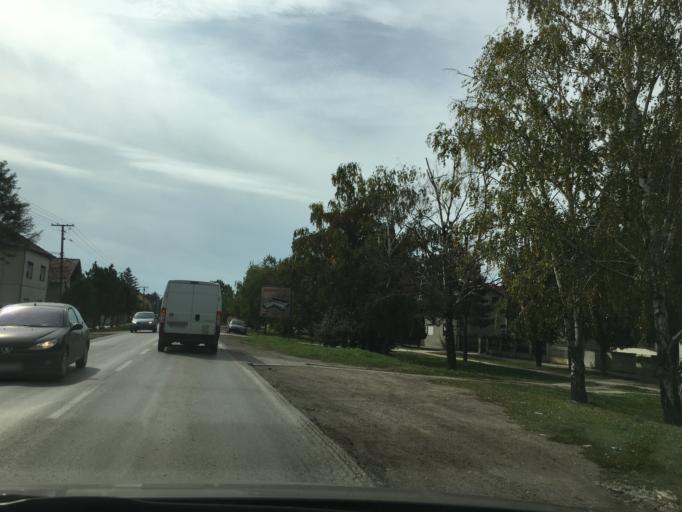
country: RS
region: Autonomna Pokrajina Vojvodina
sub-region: Juznobacki Okrug
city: Temerin
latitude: 45.3952
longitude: 19.8825
